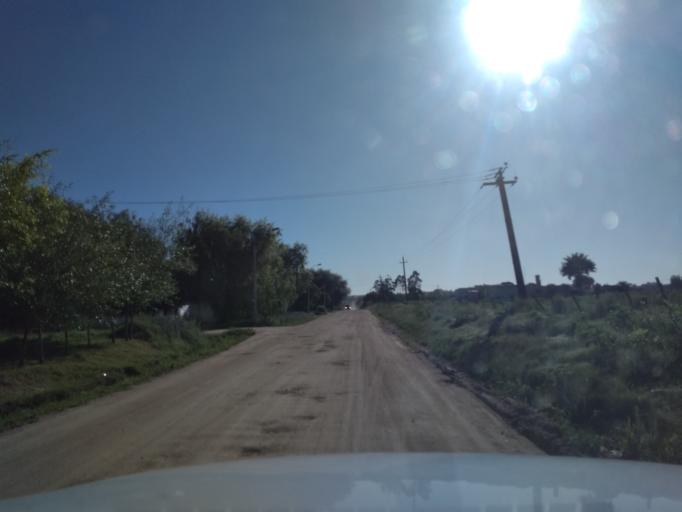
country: UY
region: Canelones
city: Pando
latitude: -34.6959
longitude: -55.9720
